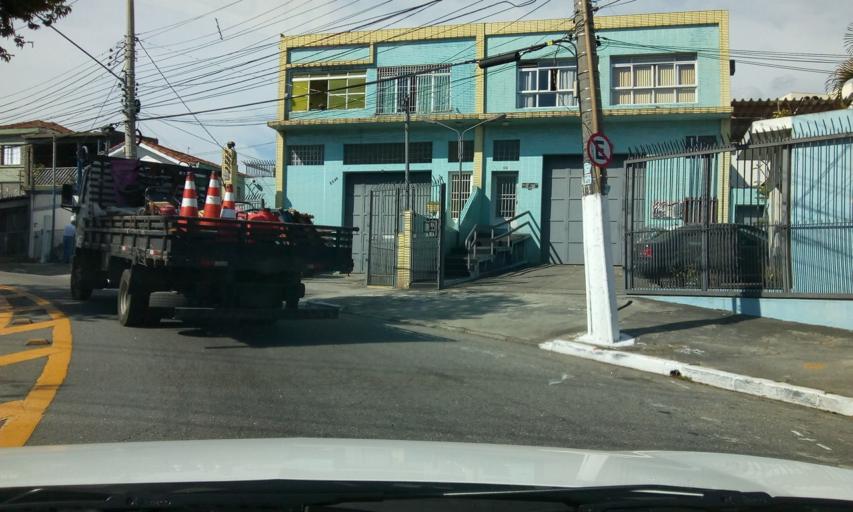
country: BR
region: Sao Paulo
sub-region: Sao Paulo
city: Sao Paulo
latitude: -23.5069
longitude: -46.6644
